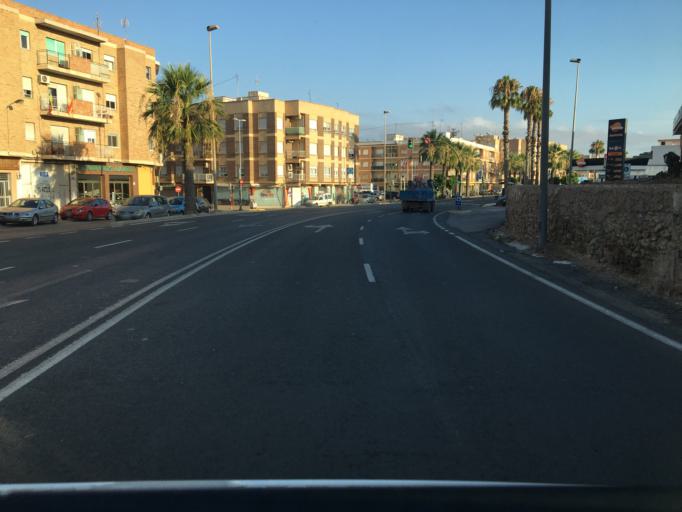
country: ES
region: Murcia
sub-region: Murcia
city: Cartagena
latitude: 37.6211
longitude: -0.9982
